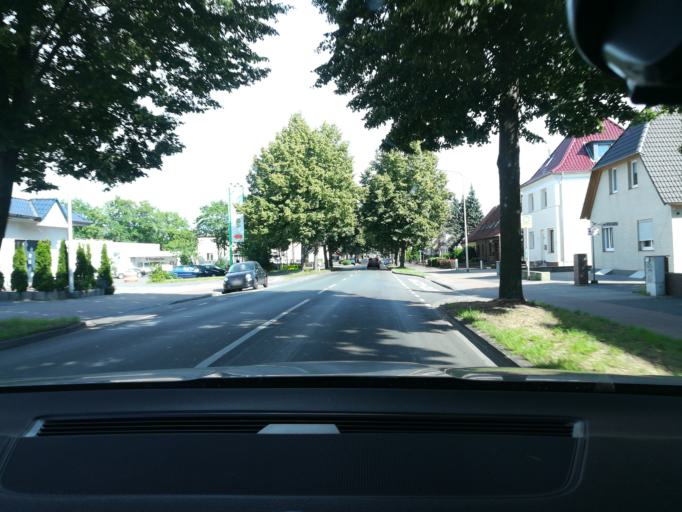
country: DE
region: North Rhine-Westphalia
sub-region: Regierungsbezirk Detmold
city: Minden
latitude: 52.3049
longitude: 8.9023
